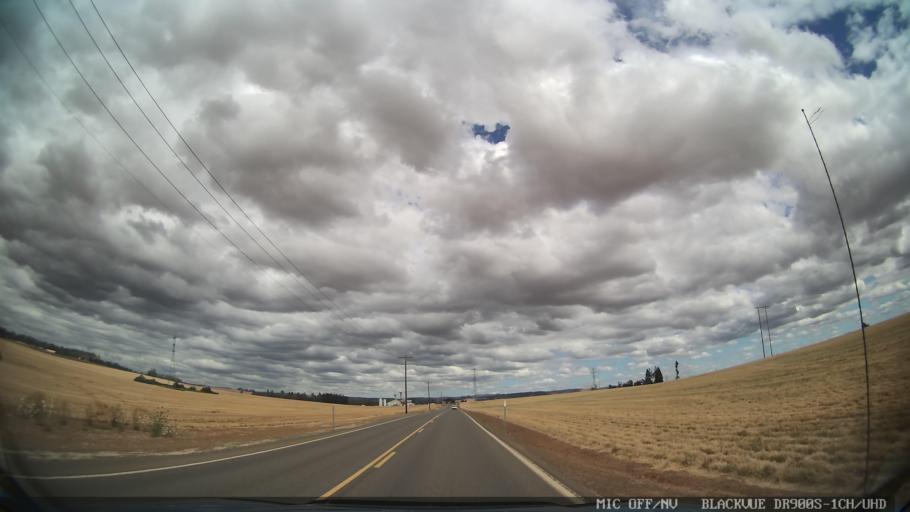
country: US
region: Oregon
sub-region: Marion County
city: Sublimity
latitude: 44.8663
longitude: -122.7987
